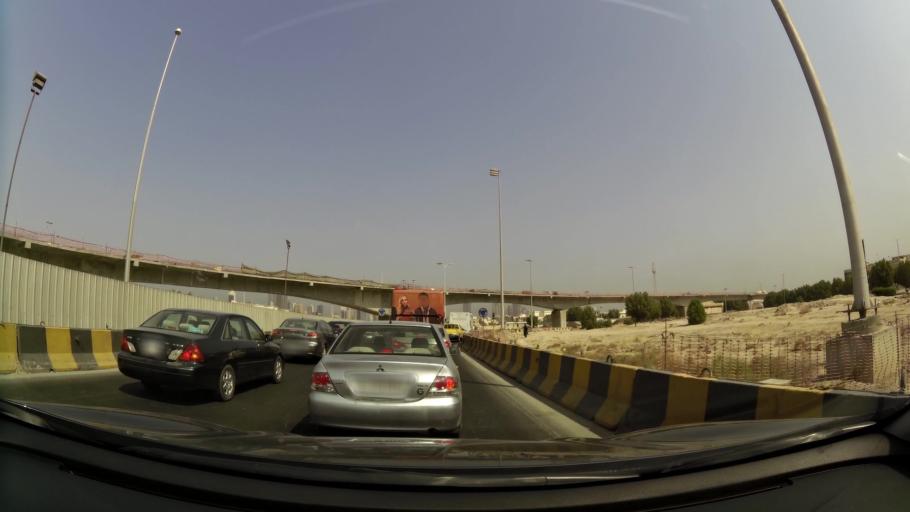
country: KW
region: Al Asimah
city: Ash Shamiyah
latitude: 29.3479
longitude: 47.9556
